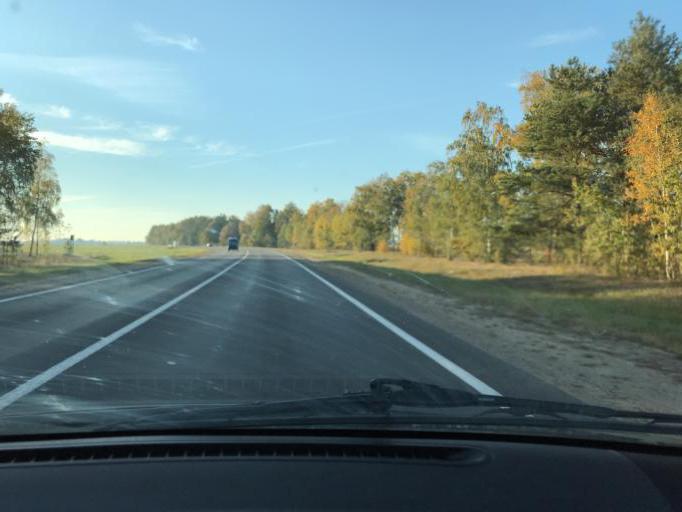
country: BY
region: Brest
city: Horad Kobryn
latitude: 52.2175
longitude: 24.5462
